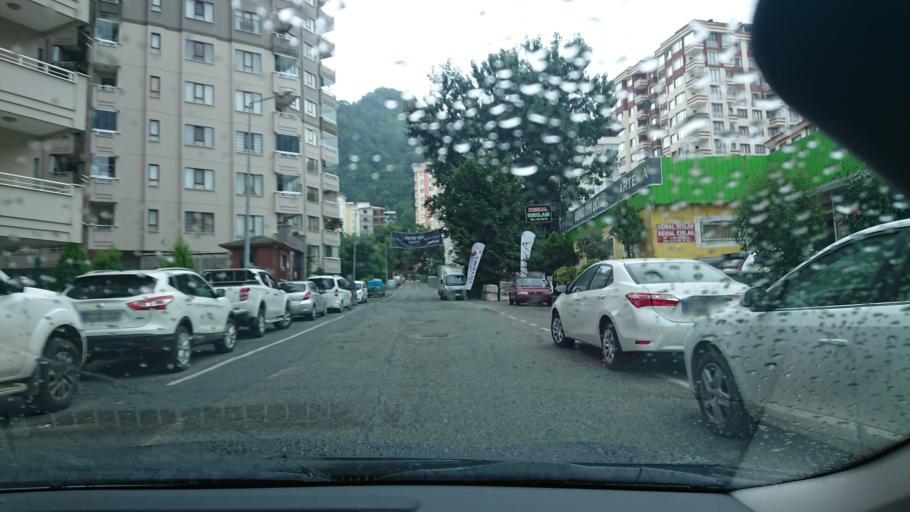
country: TR
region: Rize
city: Rize
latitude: 41.0266
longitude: 40.5461
